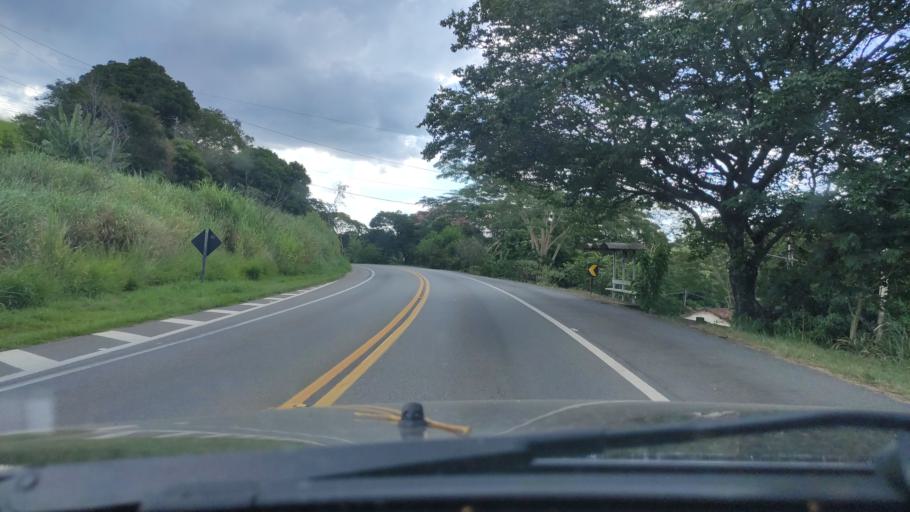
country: BR
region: Sao Paulo
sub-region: Aguas De Lindoia
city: Aguas de Lindoia
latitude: -22.4609
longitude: -46.7237
